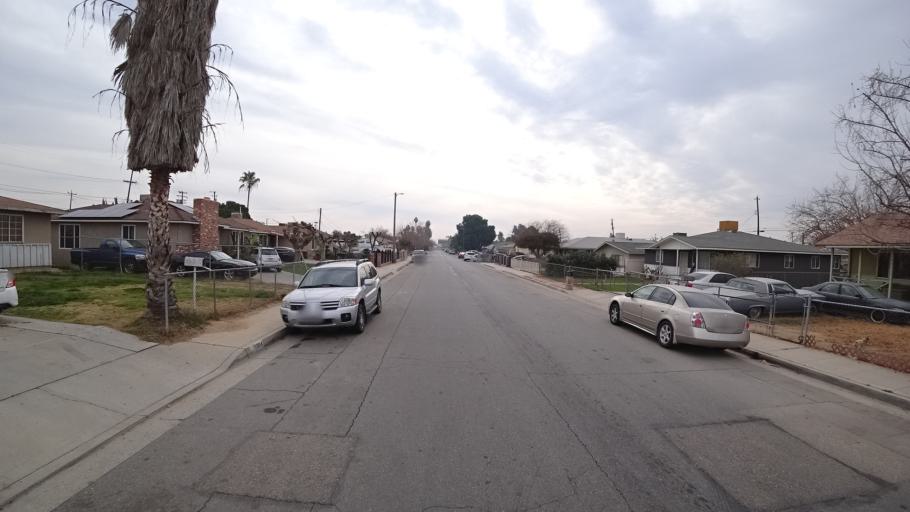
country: US
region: California
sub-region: Kern County
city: Bakersfield
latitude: 35.3458
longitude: -119.0070
